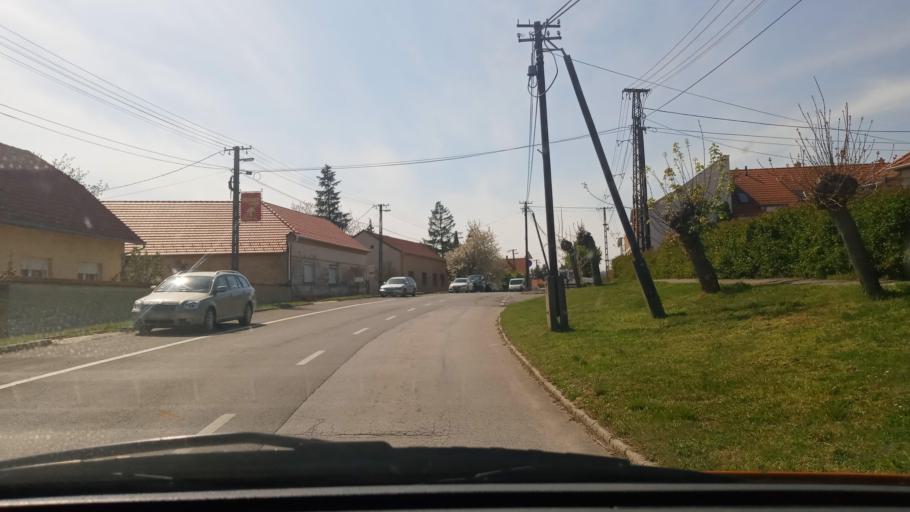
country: HU
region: Baranya
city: Pecsvarad
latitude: 46.1579
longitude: 18.4285
